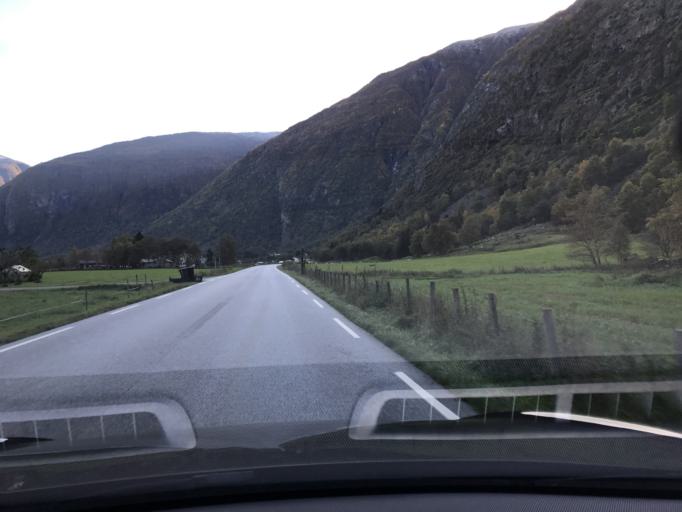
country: NO
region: Sogn og Fjordane
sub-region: Laerdal
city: Laerdalsoyri
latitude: 61.0863
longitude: 7.5112
